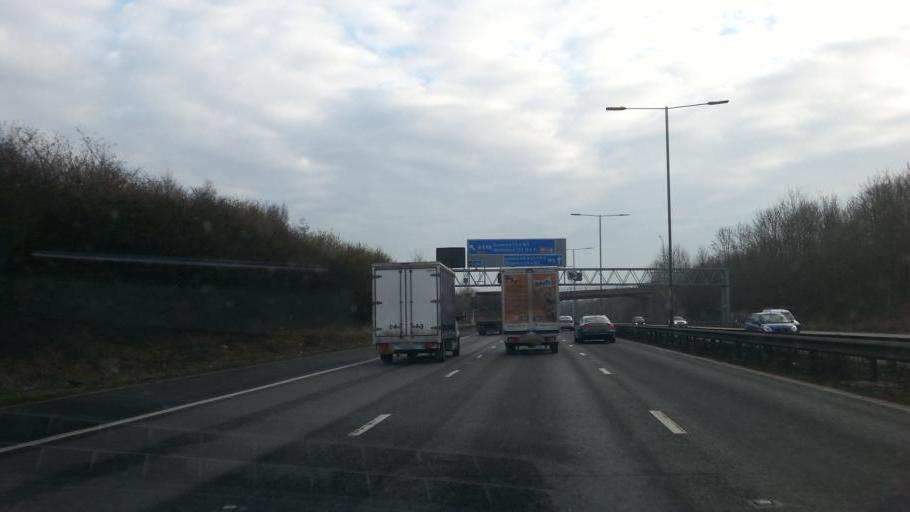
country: GB
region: England
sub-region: Solihull
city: Chelmsley Wood
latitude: 52.4934
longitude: -1.7342
